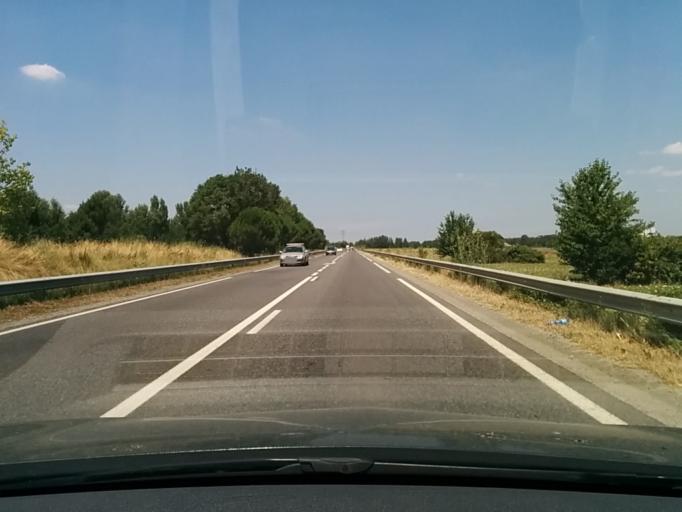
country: FR
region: Midi-Pyrenees
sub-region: Departement de la Haute-Garonne
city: Labege
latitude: 43.5175
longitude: 1.5313
